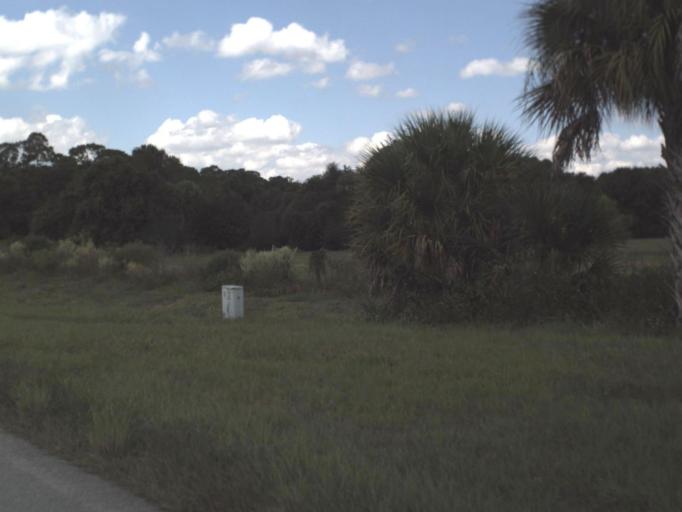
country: US
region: Florida
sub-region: Highlands County
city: Lake Placid
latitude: 27.3815
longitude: -81.1140
